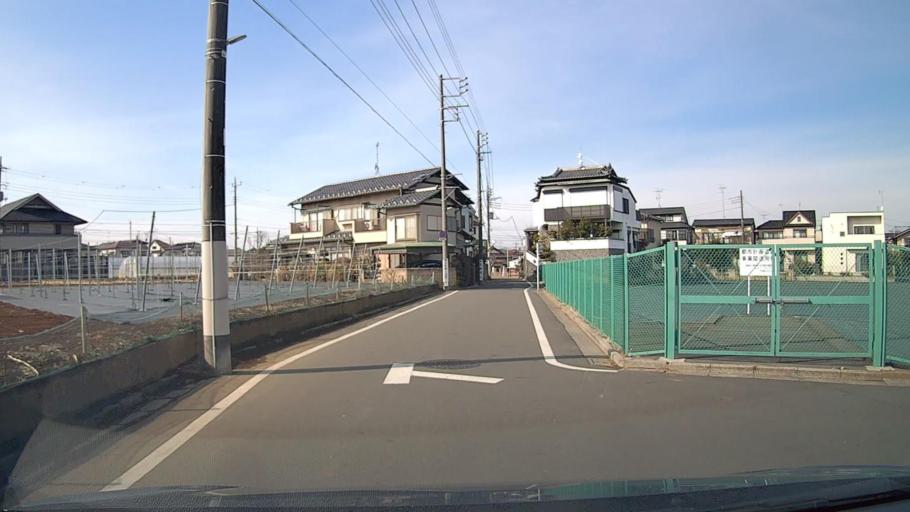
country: JP
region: Tokyo
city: Musashino
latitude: 35.7421
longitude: 139.5847
